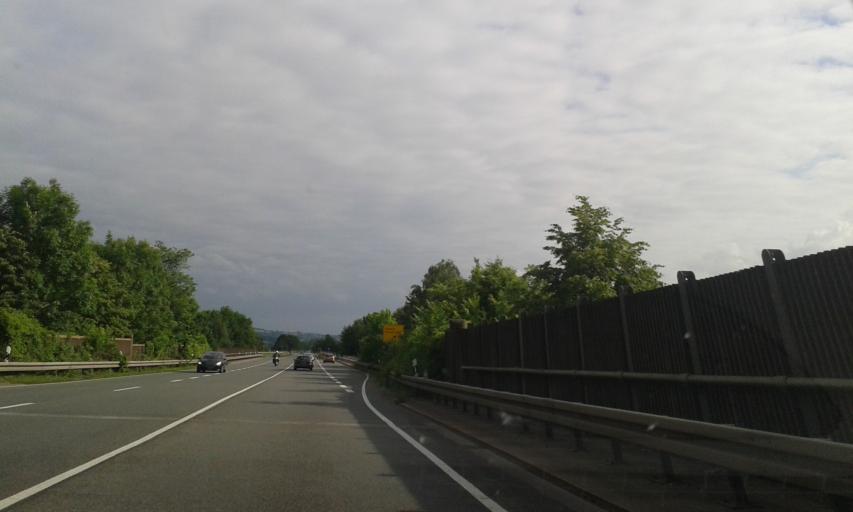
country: DE
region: Lower Saxony
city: Rinteln
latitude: 52.1987
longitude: 9.0945
